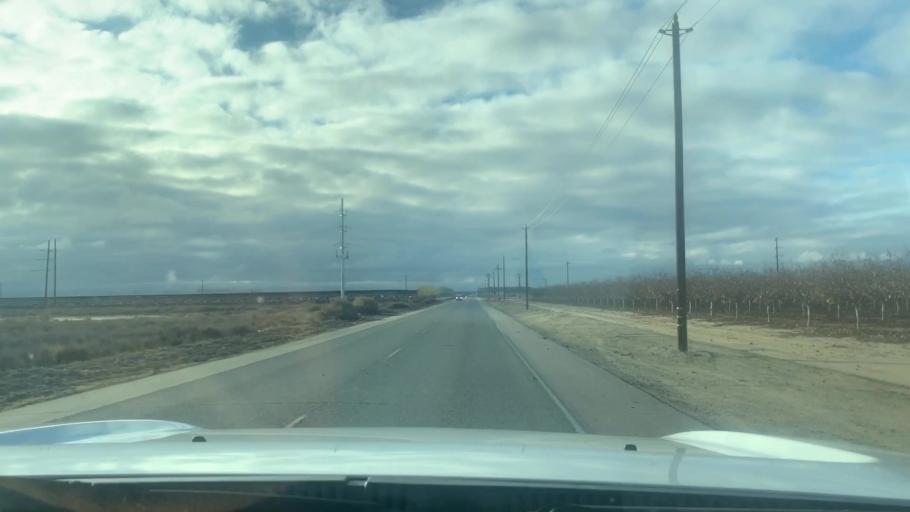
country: US
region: California
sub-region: Kern County
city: Buttonwillow
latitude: 35.5006
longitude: -119.4457
